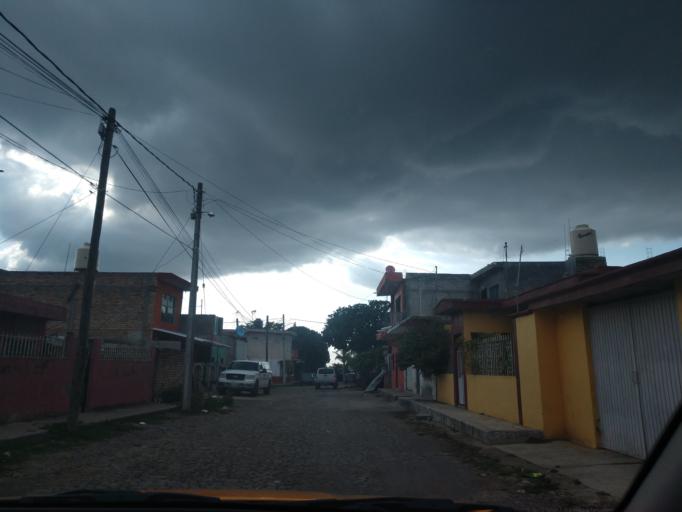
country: MX
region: Nayarit
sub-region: Tepic
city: La Corregidora
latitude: 21.4498
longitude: -104.8134
